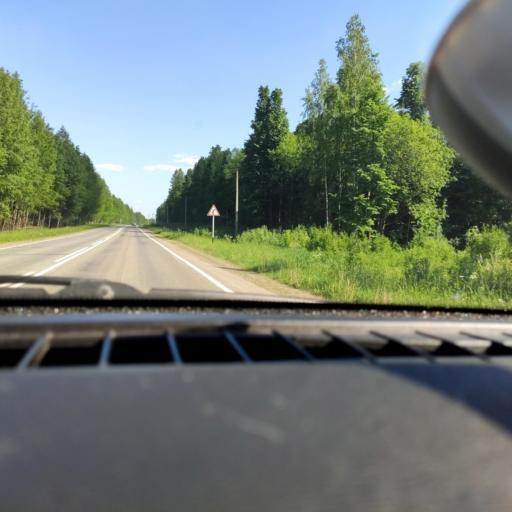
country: RU
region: Perm
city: Perm
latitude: 58.2120
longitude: 56.1835
